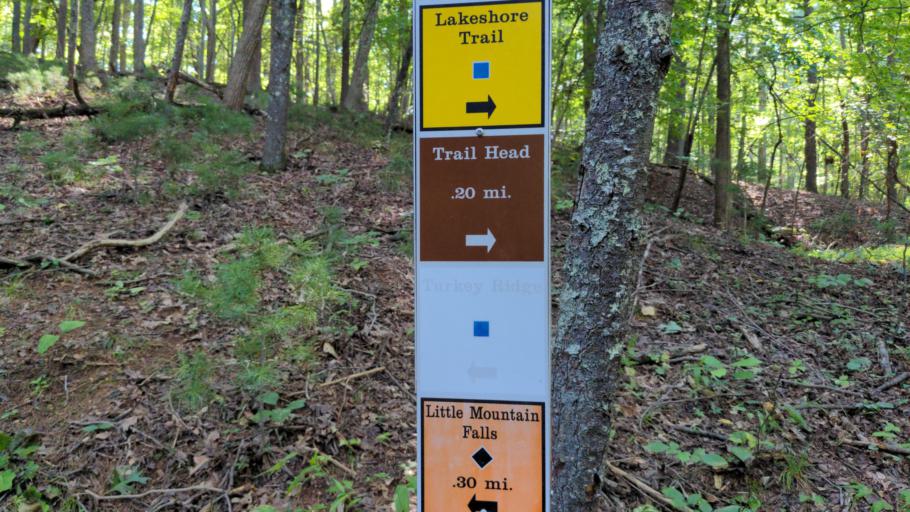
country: US
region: Virginia
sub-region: Henry County
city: Bassett
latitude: 36.7957
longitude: -80.1085
